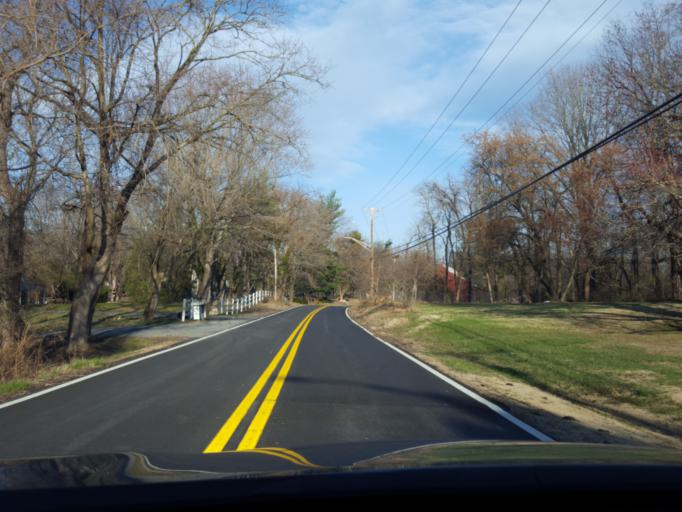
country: US
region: Maryland
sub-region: Anne Arundel County
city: Deale
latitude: 38.7540
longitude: -76.5712
